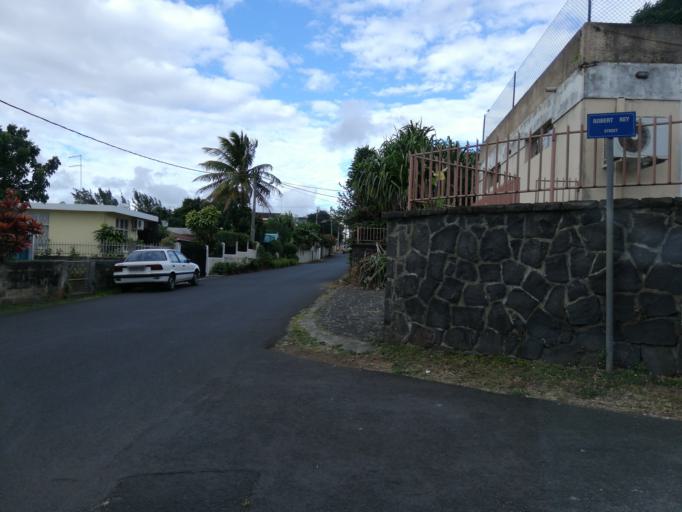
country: MU
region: Black River
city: Gros Cailloux
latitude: -20.2332
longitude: 57.4560
